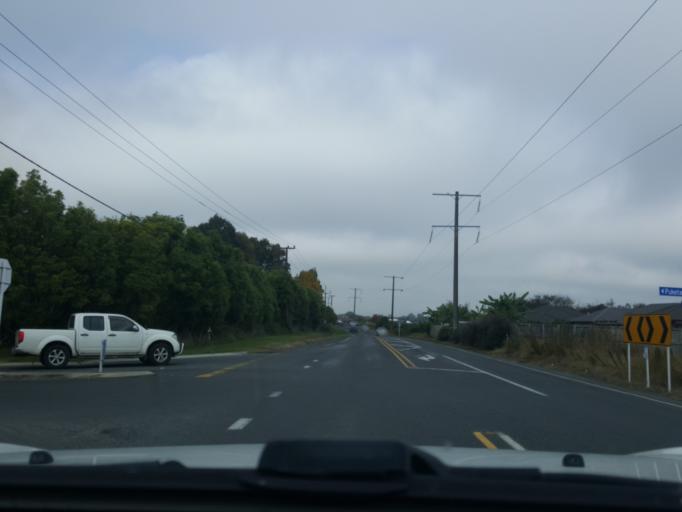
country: NZ
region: Waikato
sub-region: Hamilton City
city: Hamilton
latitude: -37.7387
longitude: 175.2890
